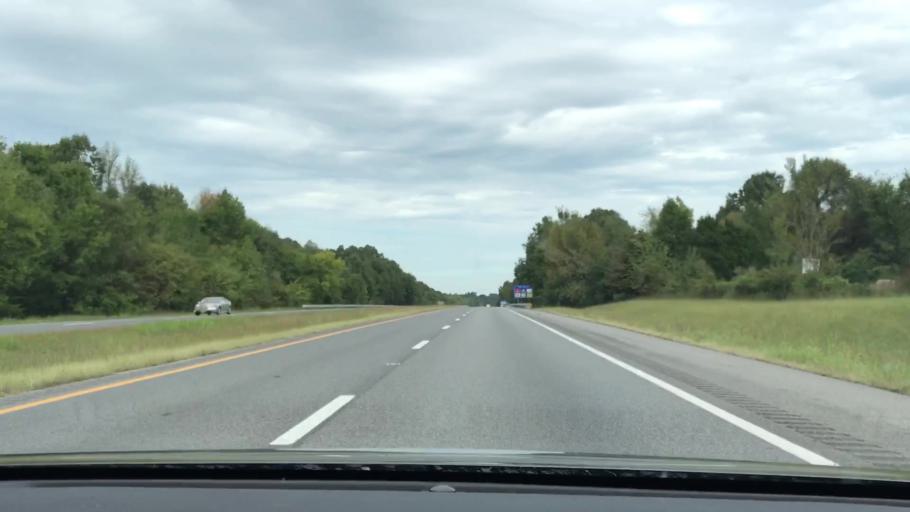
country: US
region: Kentucky
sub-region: Marshall County
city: Benton
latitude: 36.9070
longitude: -88.3483
